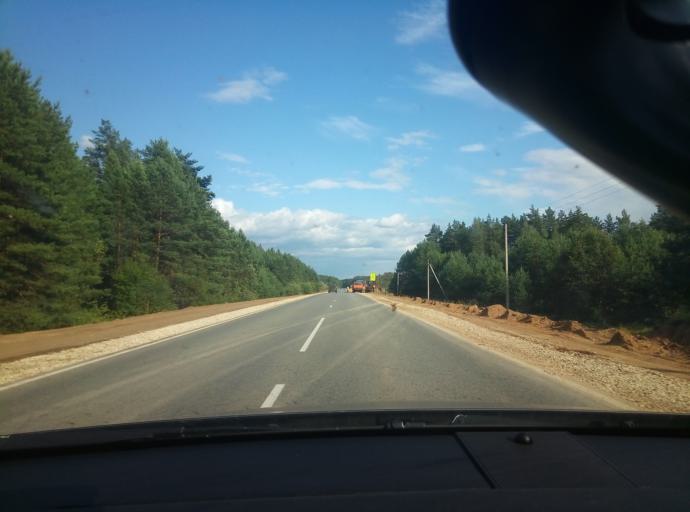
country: RU
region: Kaluga
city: Yukhnov
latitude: 54.7212
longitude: 35.2212
